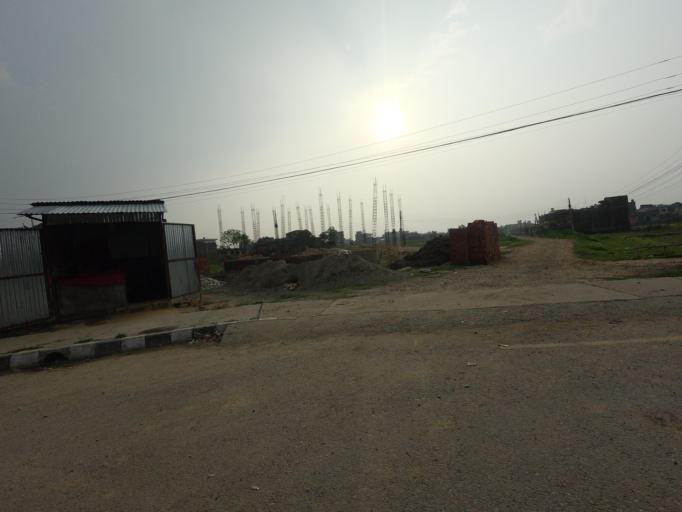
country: NP
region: Western Region
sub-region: Lumbini Zone
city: Bhairahawa
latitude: 27.5035
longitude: 83.4434
